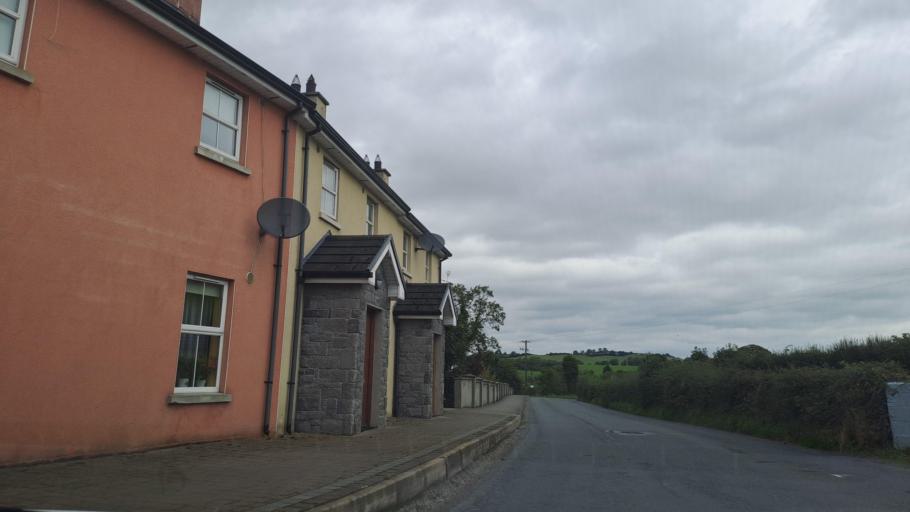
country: IE
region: Ulster
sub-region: An Cabhan
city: Bailieborough
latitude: 53.9946
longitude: -6.8937
